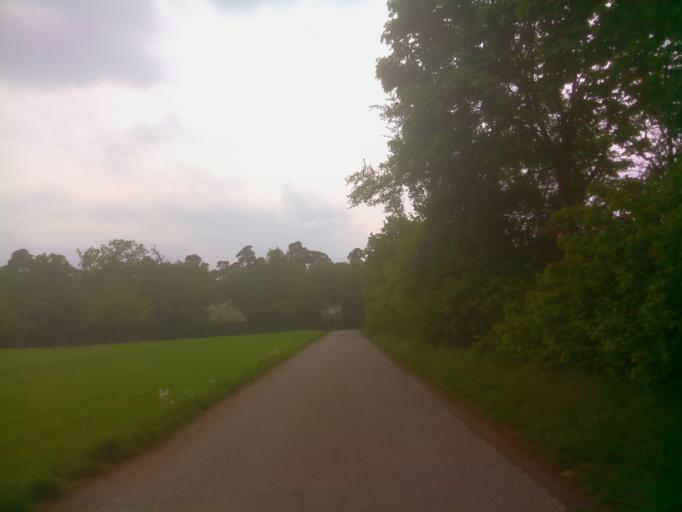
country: DE
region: Baden-Wuerttemberg
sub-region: Karlsruhe Region
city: Oftersheim
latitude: 49.3609
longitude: 8.6056
